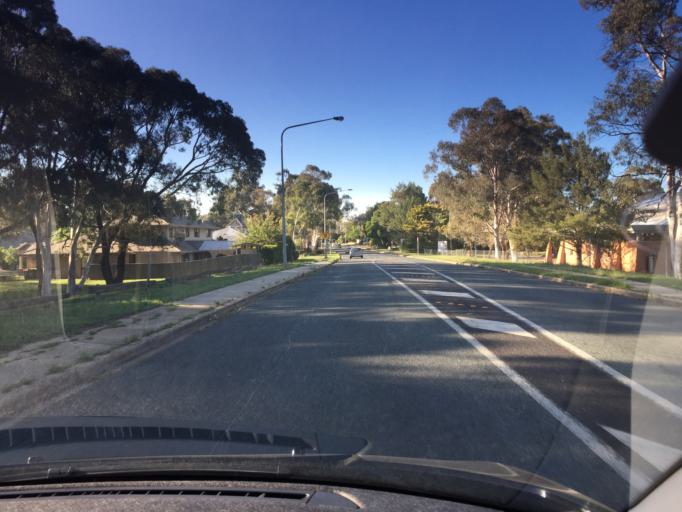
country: AU
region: Australian Capital Territory
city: Kaleen
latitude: -35.2223
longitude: 149.1111
